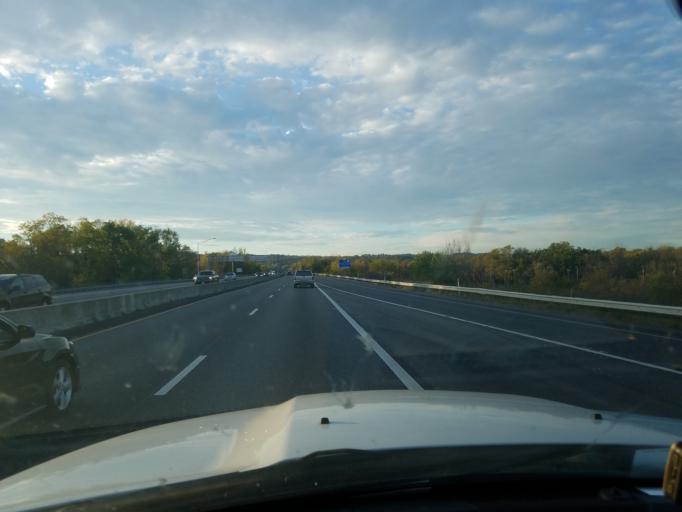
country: US
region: Indiana
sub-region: Floyd County
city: New Albany
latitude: 38.2867
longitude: -85.8306
